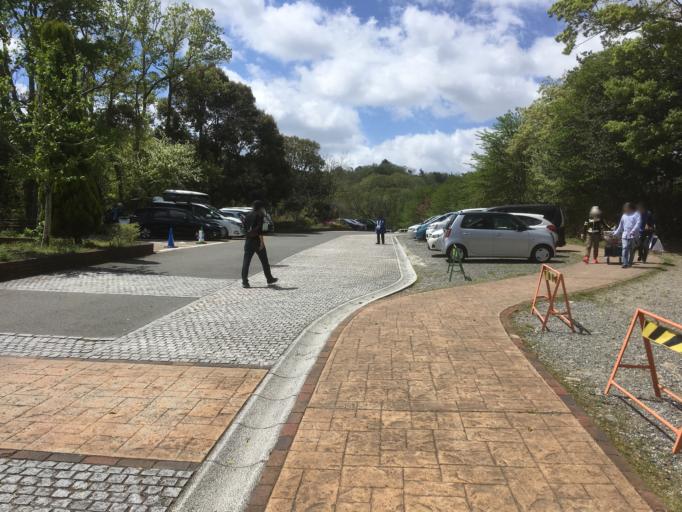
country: JP
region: Nara
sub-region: Ikoma-shi
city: Ikoma
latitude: 34.7013
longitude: 135.6767
